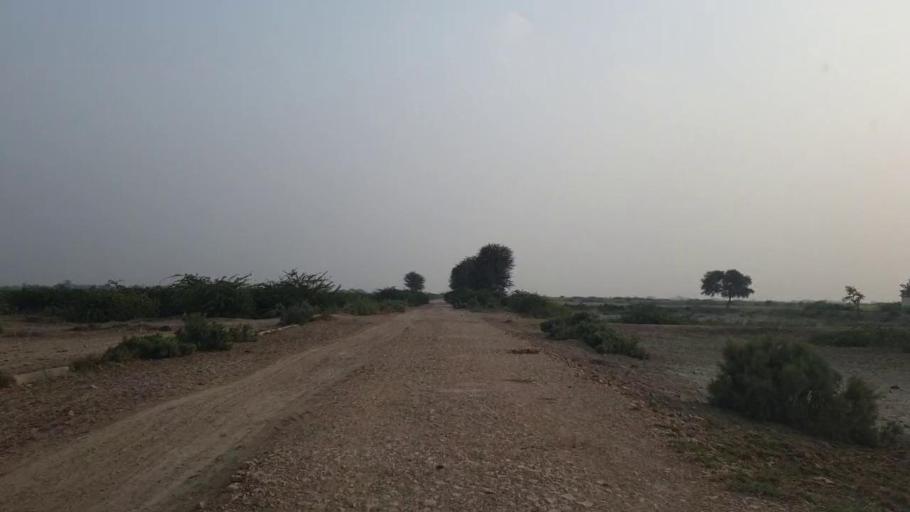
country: PK
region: Sindh
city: Mirpur Batoro
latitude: 24.6481
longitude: 68.3727
